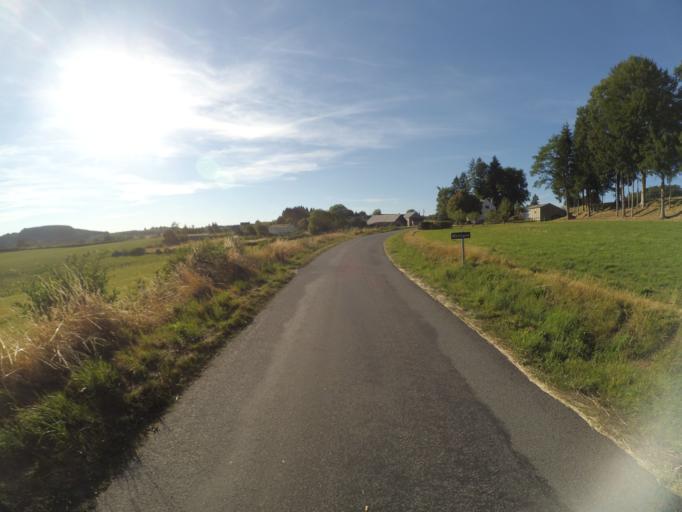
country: FR
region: Limousin
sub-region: Departement de la Creuse
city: Banize
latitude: 45.7338
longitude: 2.0406
